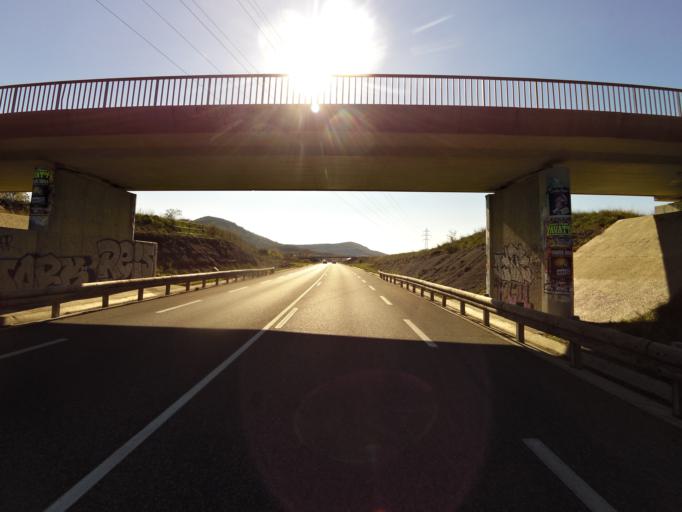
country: FR
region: Rhone-Alpes
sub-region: Departement de l'Ardeche
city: Saint-Sernin
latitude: 44.5800
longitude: 4.3819
